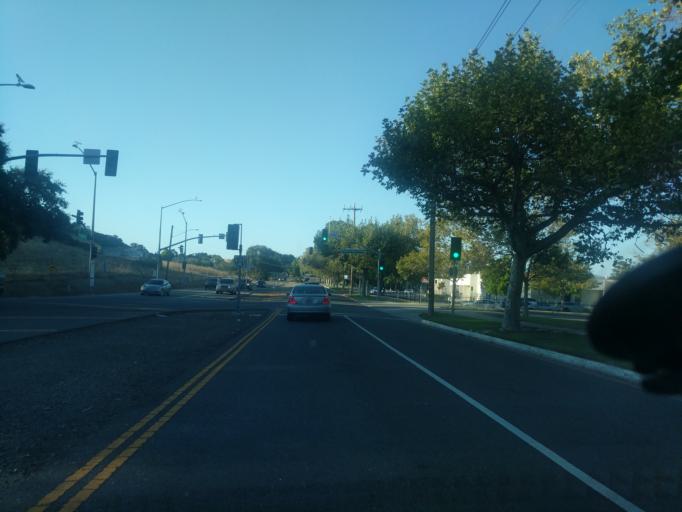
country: US
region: California
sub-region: Alameda County
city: Dublin
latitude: 37.6705
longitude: -121.9196
